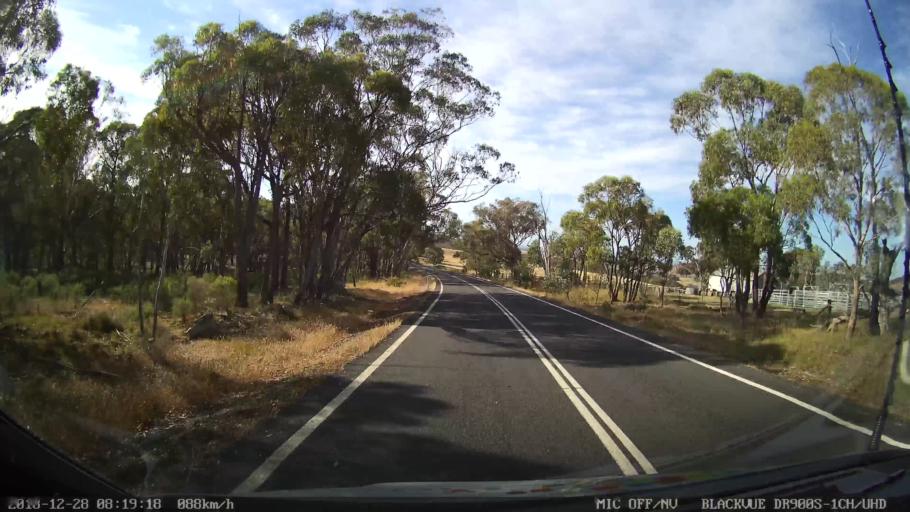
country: AU
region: New South Wales
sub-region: Blayney
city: Blayney
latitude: -33.8573
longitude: 149.3507
